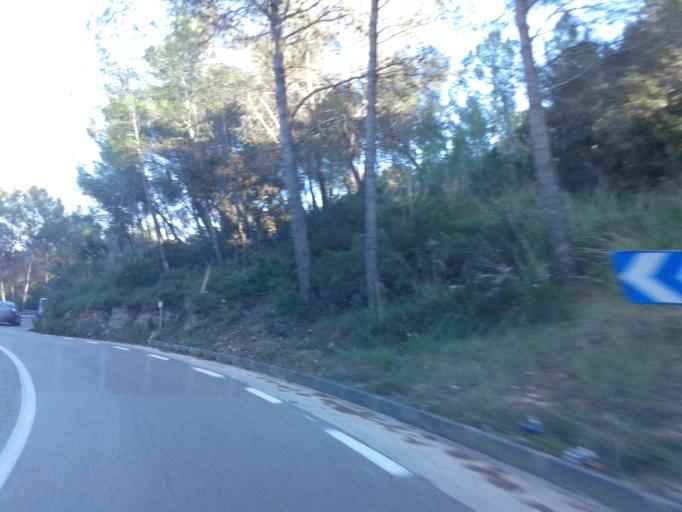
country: ES
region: Catalonia
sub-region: Provincia de Barcelona
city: Avinyonet del Penedes
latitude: 41.3170
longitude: 1.7637
